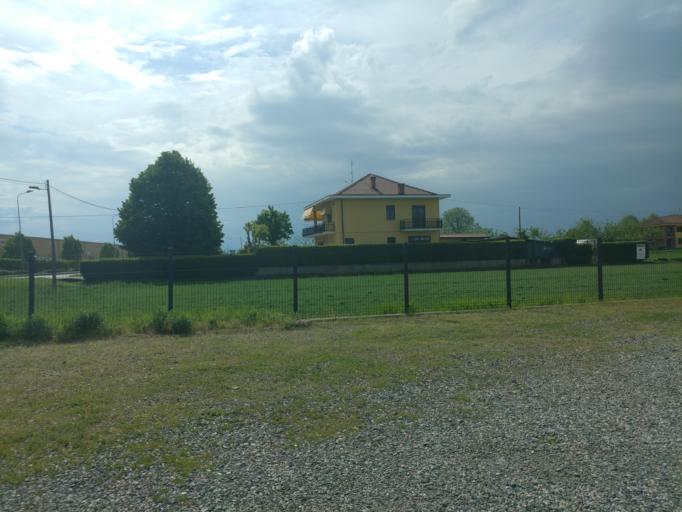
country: IT
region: Piedmont
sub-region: Provincia di Torino
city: Pancalieri
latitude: 44.8357
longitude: 7.5784
